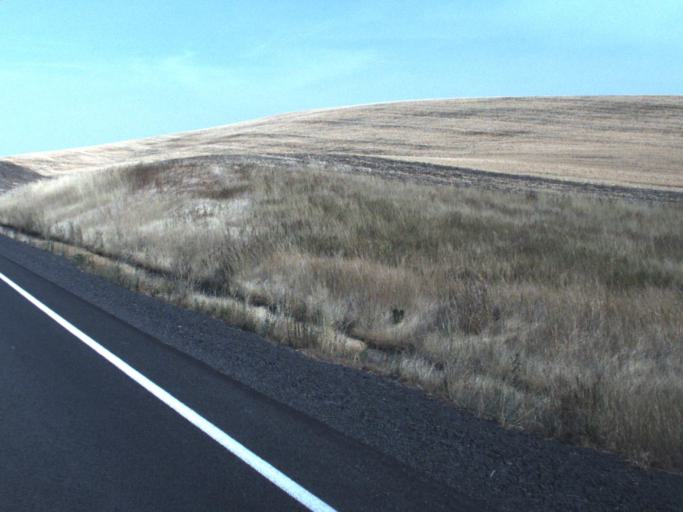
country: US
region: Washington
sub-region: Whitman County
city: Pullman
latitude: 46.8179
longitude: -117.1170
